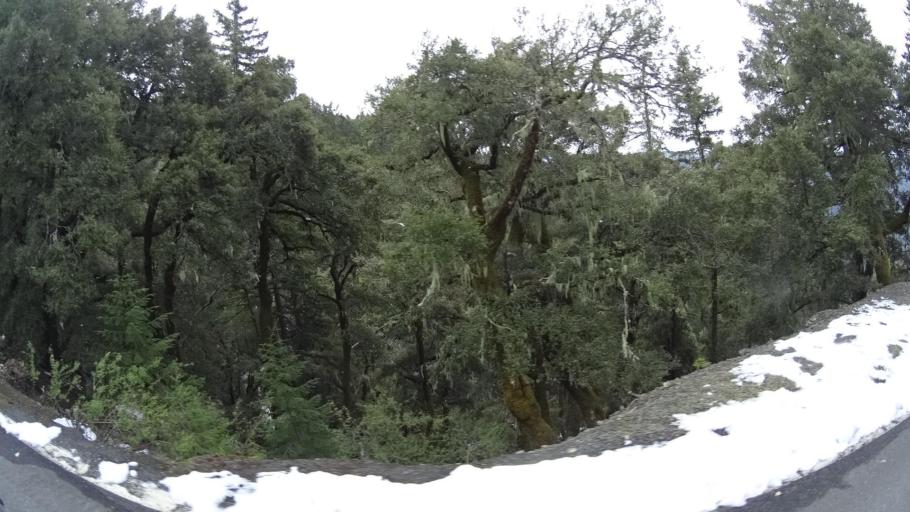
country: US
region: California
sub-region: Humboldt County
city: Willow Creek
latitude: 40.8789
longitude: -123.7590
